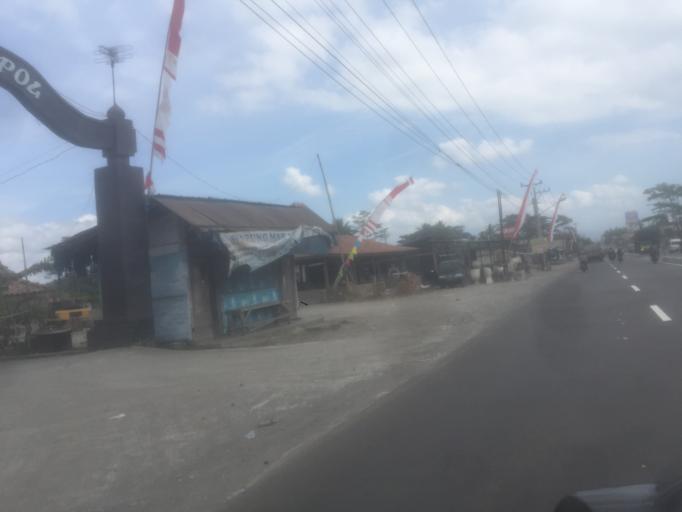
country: ID
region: Central Java
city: Muntilan
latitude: -7.6053
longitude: 110.3010
